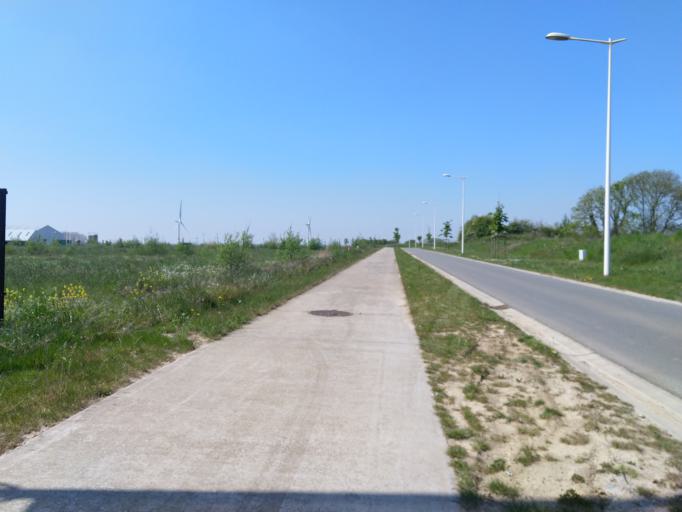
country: BE
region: Wallonia
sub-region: Province du Hainaut
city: Soignies
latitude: 50.5939
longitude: 4.0891
